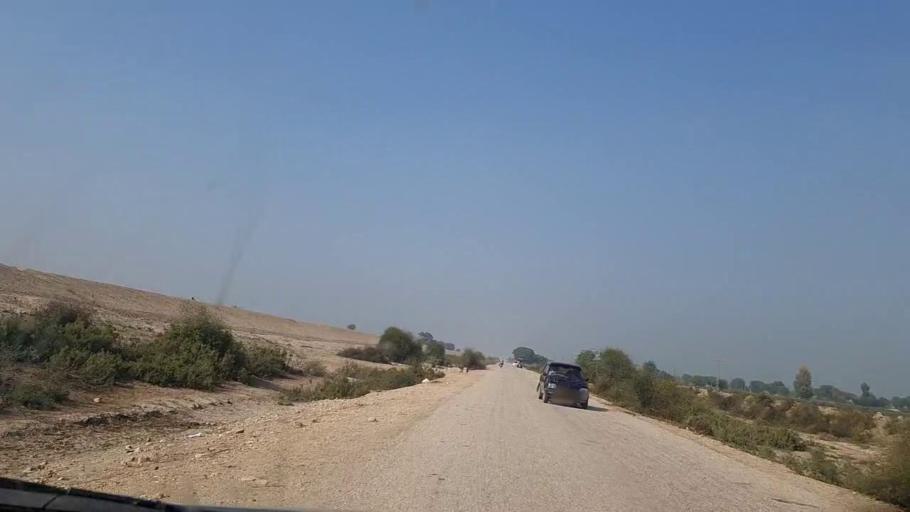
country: PK
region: Sindh
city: Moro
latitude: 26.7124
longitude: 67.9246
